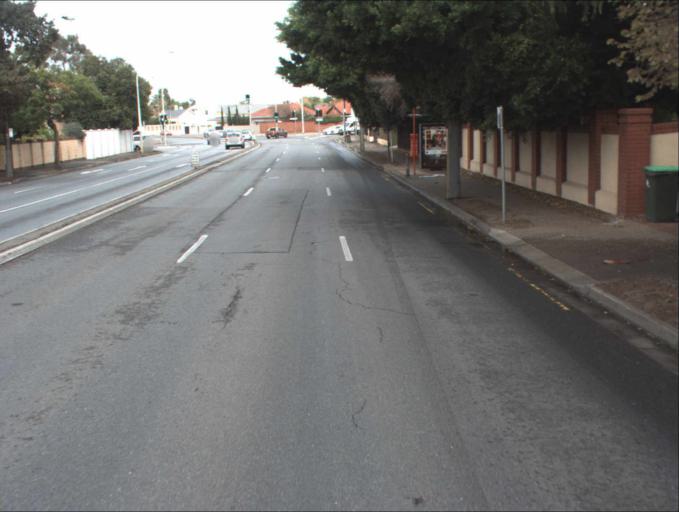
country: AU
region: South Australia
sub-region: Prospect
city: Prospect
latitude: -34.8923
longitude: 138.6103
